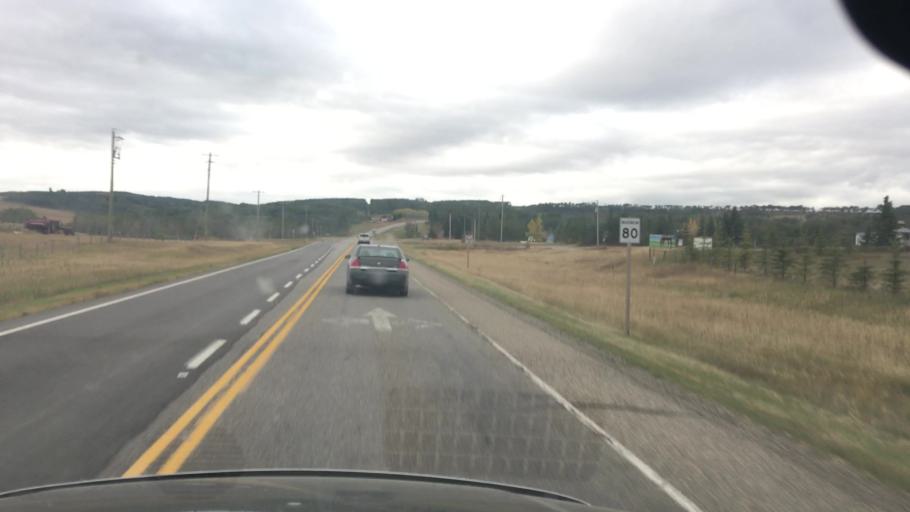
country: CA
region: Alberta
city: Cochrane
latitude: 51.3758
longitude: -114.4702
